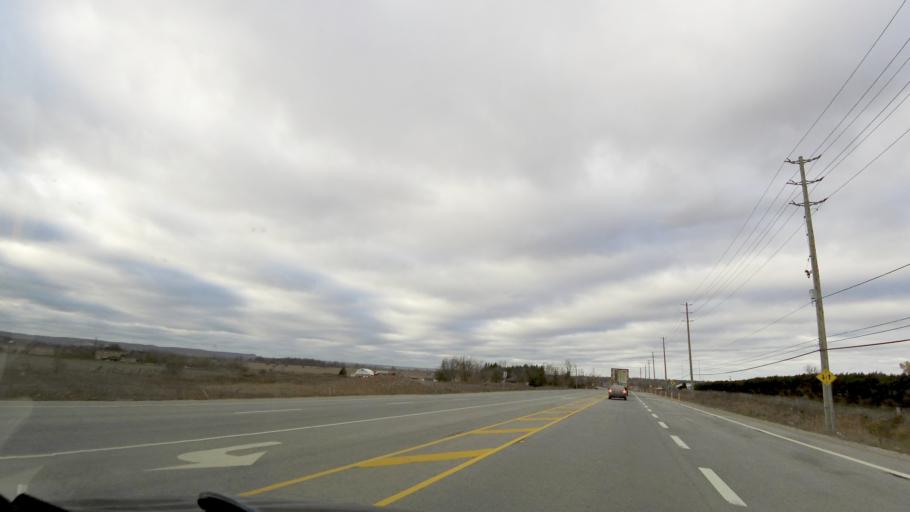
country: CA
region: Ontario
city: Burlington
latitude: 43.4631
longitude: -79.8064
